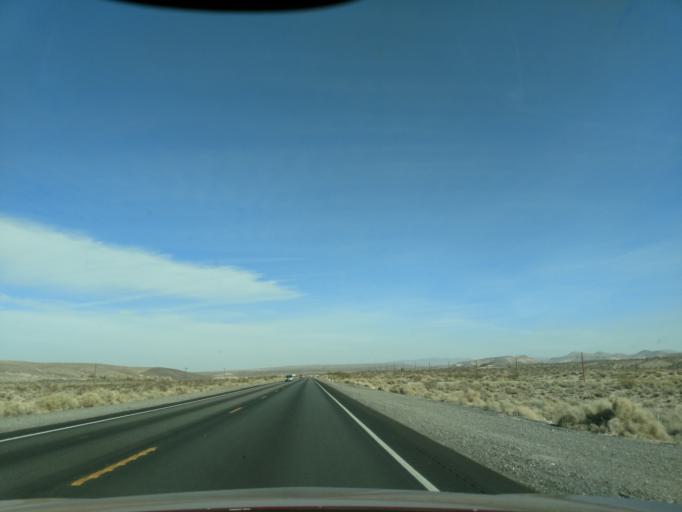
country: US
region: Nevada
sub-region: Nye County
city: Beatty
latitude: 36.9291
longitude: -116.7344
